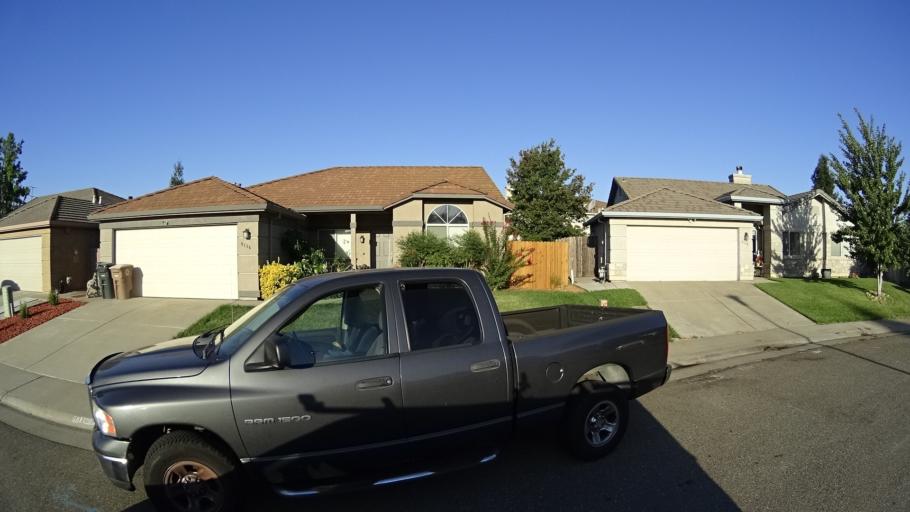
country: US
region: California
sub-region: Sacramento County
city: Laguna
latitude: 38.4266
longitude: -121.4542
